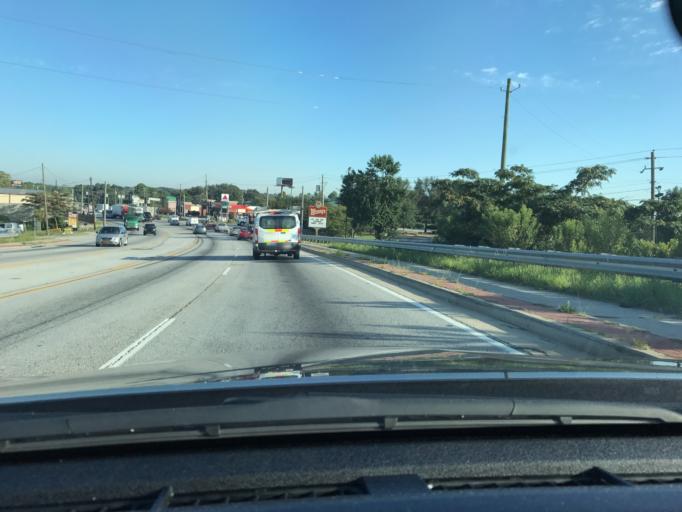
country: US
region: Georgia
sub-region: Clayton County
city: Forest Park
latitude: 33.6283
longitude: -84.3846
